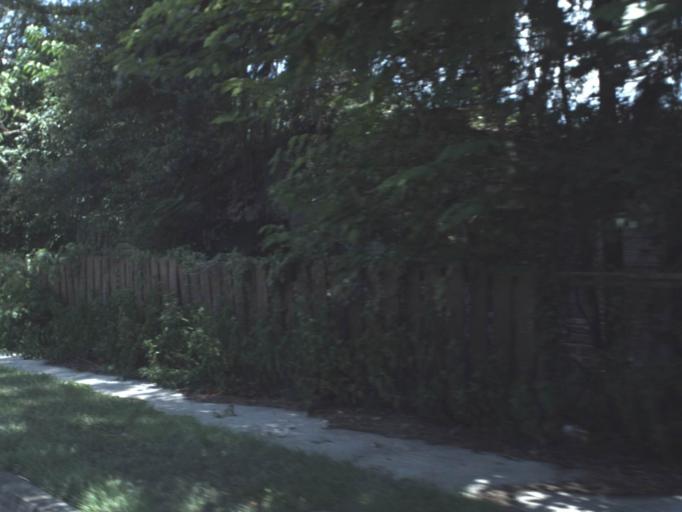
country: US
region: Florida
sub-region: Taylor County
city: Perry
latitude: 30.0933
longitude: -83.5415
